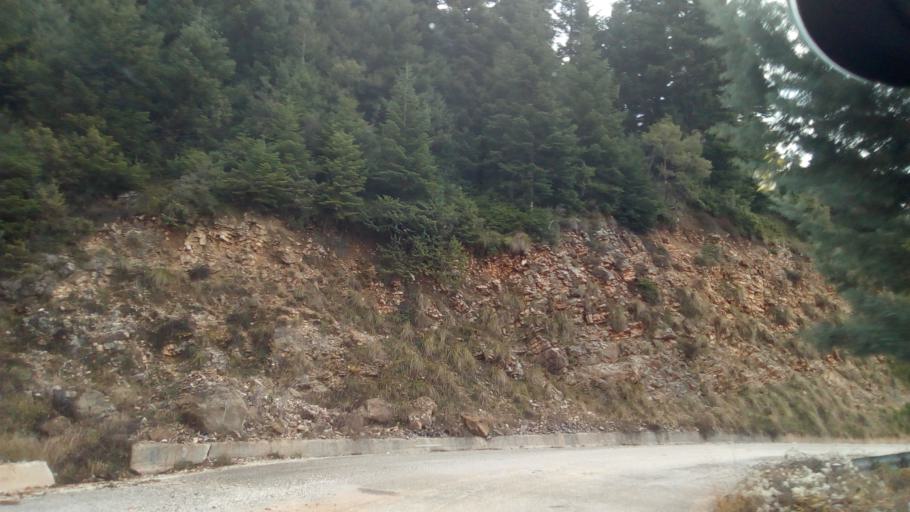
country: GR
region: West Greece
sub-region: Nomos Aitolias kai Akarnanias
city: Thermo
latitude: 38.6834
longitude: 21.8725
